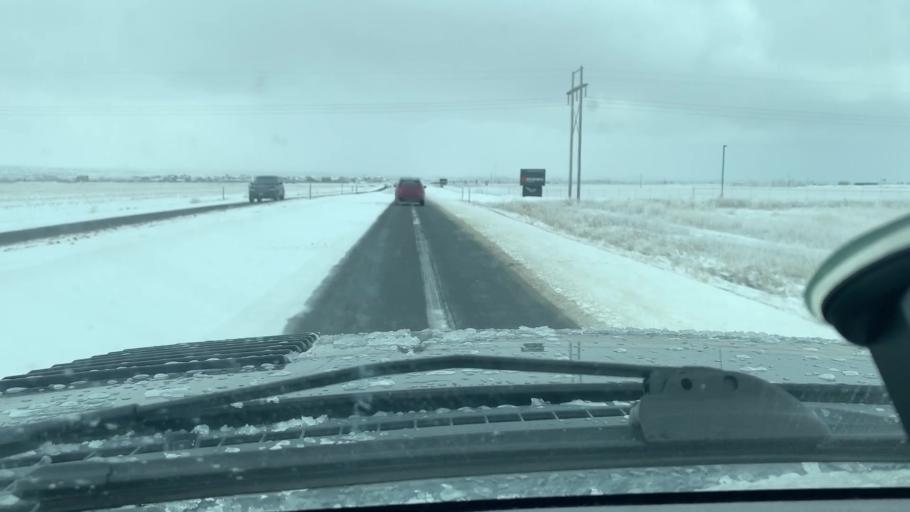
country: US
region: Colorado
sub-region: Weld County
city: Mead
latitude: 40.1978
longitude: -104.9702
